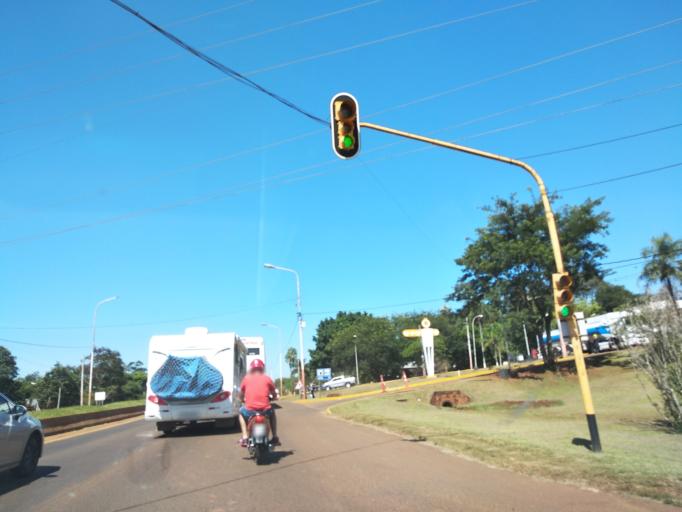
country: AR
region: Misiones
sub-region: Departamento de Iguazu
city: Puerto Iguazu
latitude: -25.6146
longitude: -54.5590
